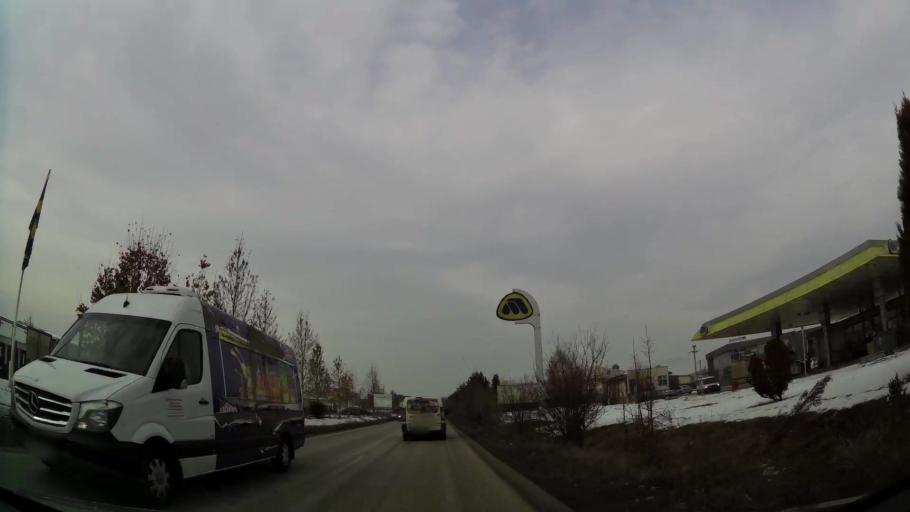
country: MK
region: Suto Orizari
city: Suto Orizare
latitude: 42.0320
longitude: 21.4040
